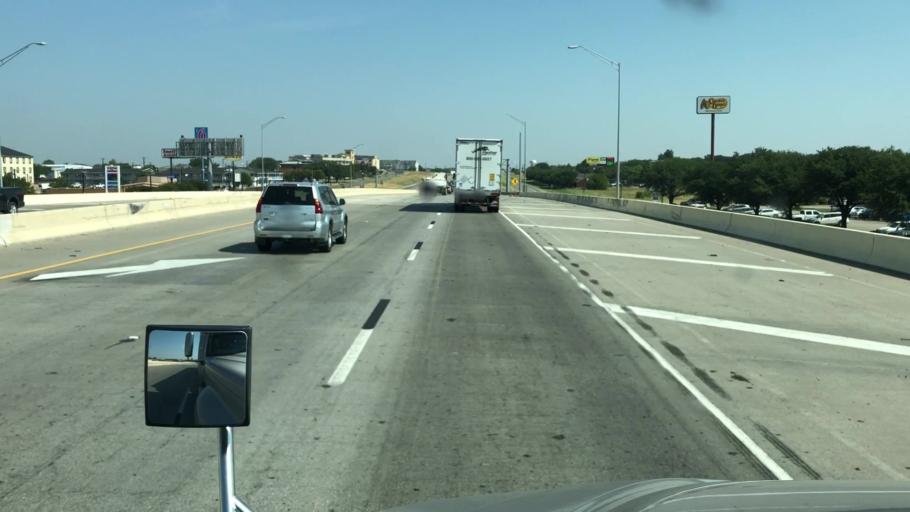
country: US
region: Texas
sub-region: Denton County
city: Denton
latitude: 33.2300
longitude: -97.1739
